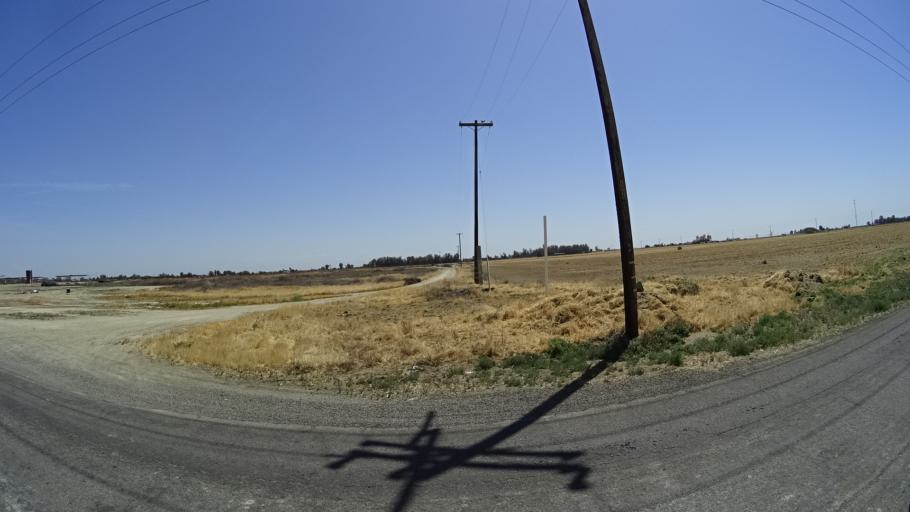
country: US
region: California
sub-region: Kings County
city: Lemoore
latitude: 36.2440
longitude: -119.7986
